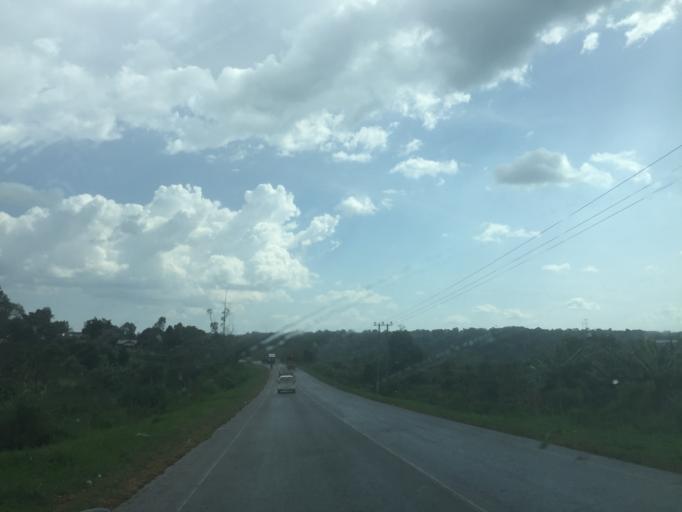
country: UG
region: Central Region
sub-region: Luwero District
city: Wobulenzi
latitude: 0.5653
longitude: 32.5291
